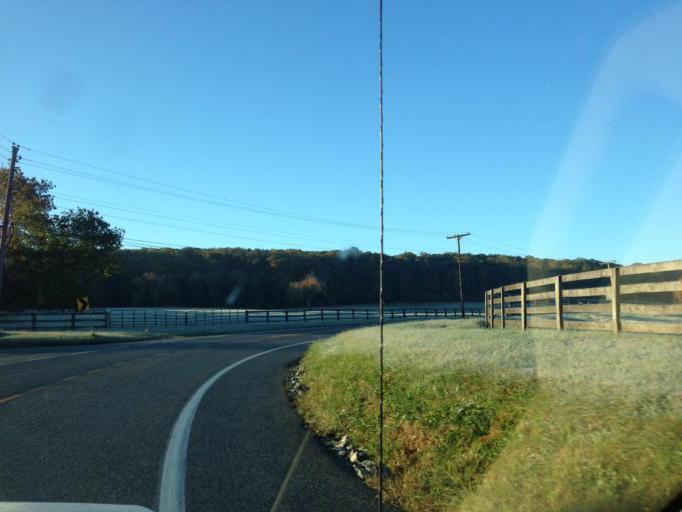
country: US
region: Maryland
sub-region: Baltimore County
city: Owings Mills
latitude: 39.4935
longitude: -76.7395
